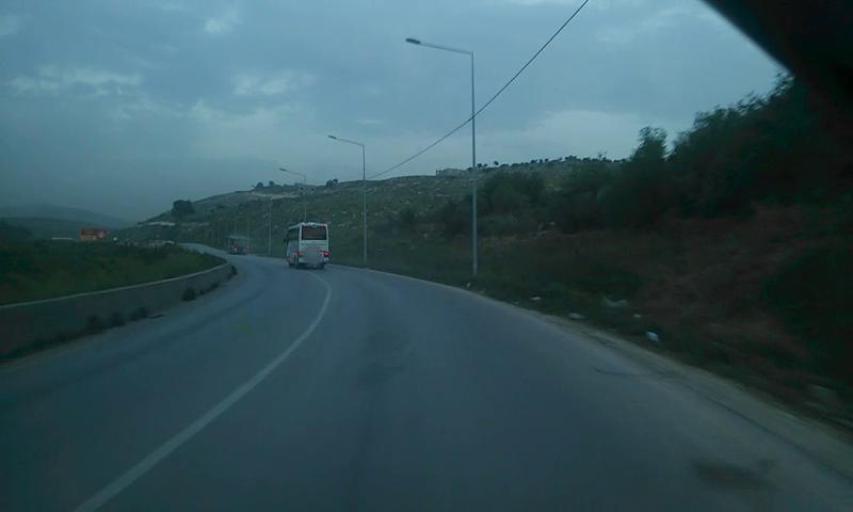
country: PS
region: West Bank
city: Iktabah
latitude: 32.3179
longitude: 35.0677
